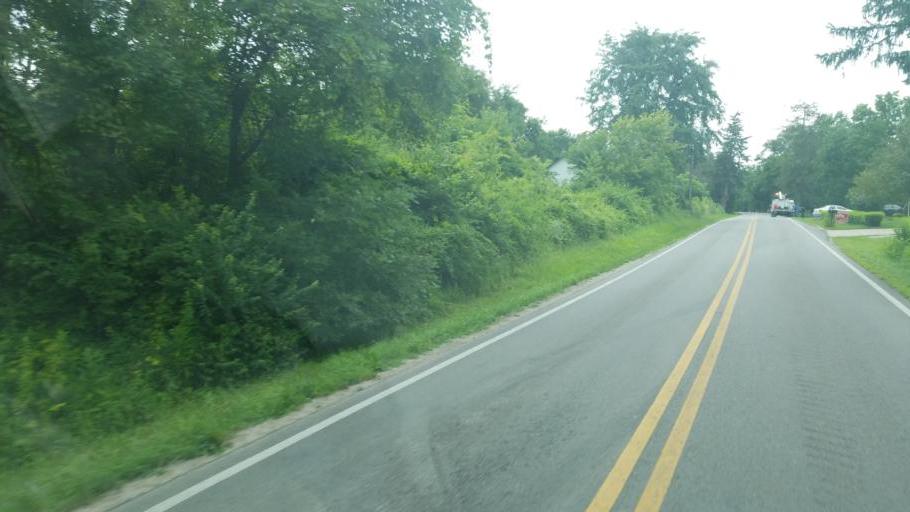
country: US
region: Ohio
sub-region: Delaware County
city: Ashley
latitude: 40.3980
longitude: -82.9472
